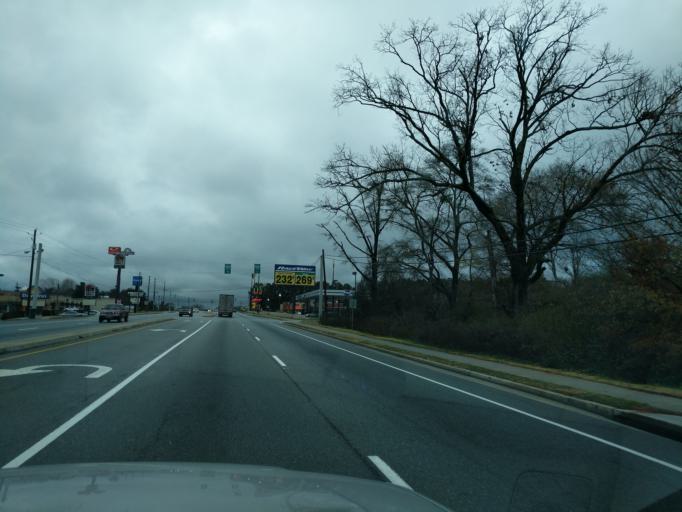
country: US
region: Georgia
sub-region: Franklin County
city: Lavonia
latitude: 34.4449
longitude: -83.1176
